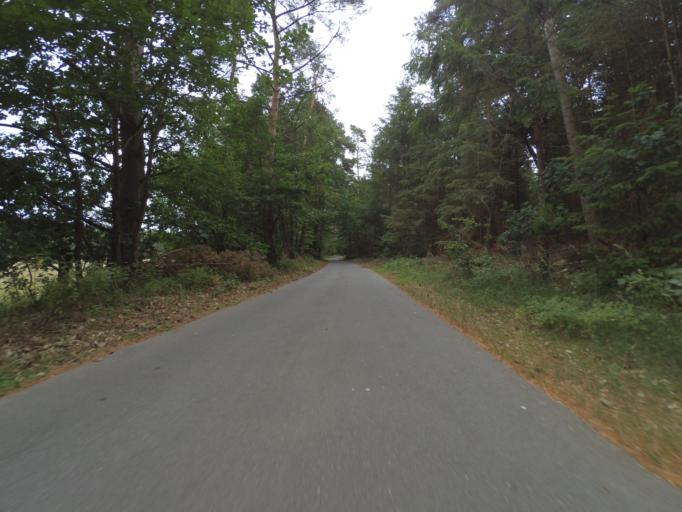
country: DE
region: Mecklenburg-Vorpommern
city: Grabowhofe
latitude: 53.5281
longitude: 12.5830
